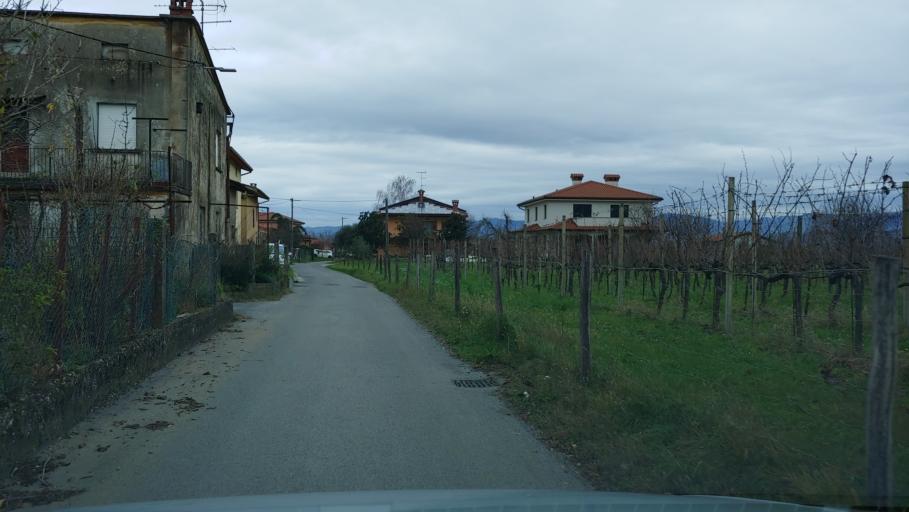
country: SI
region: Miren-Kostanjevica
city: Miren
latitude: 45.8888
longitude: 13.6135
